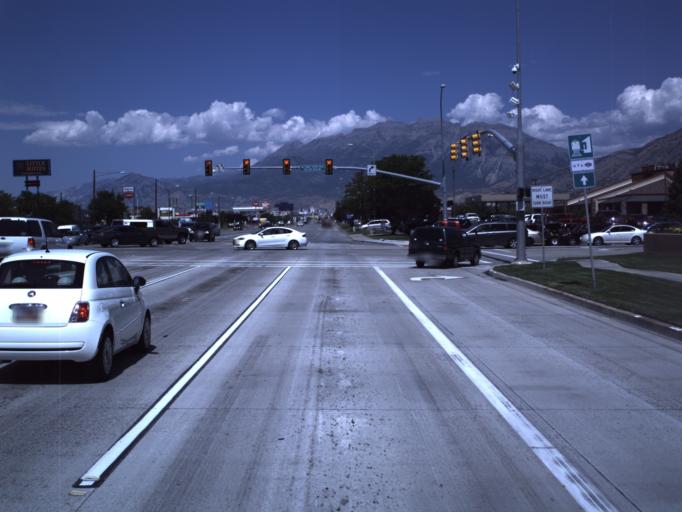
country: US
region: Utah
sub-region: Utah County
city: Provo
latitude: 40.2142
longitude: -111.6588
